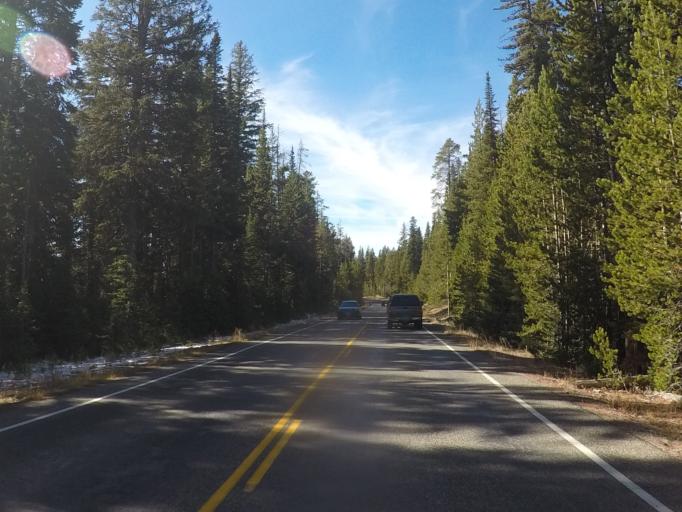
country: US
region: Montana
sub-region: Gallatin County
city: West Yellowstone
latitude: 44.4629
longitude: -110.4774
